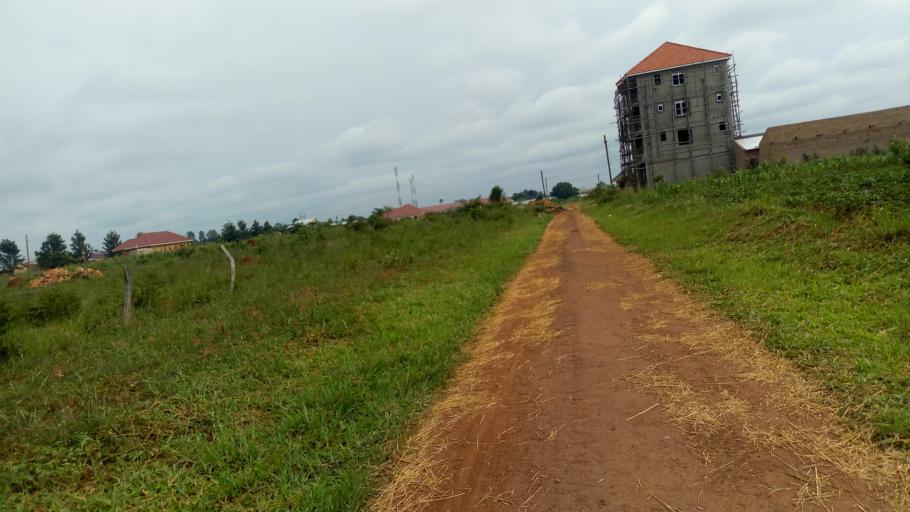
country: UG
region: Western Region
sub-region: Kiryandongo District
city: Kiryandongo
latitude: 1.8017
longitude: 32.0138
